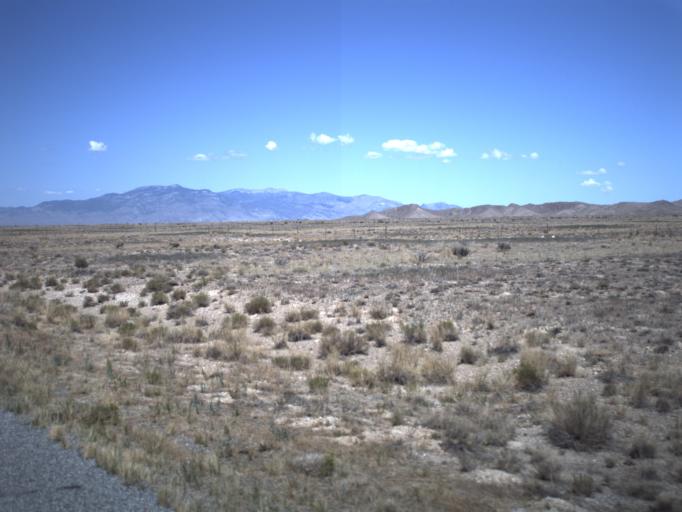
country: US
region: Nevada
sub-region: White Pine County
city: McGill
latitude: 39.0399
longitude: -113.8244
